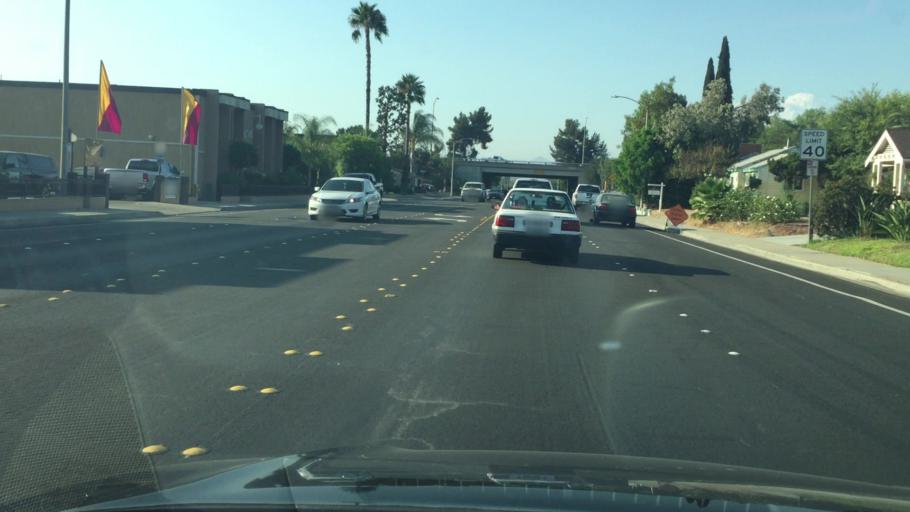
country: US
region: California
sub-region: San Diego County
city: El Cajon
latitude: 32.8014
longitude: -116.9581
